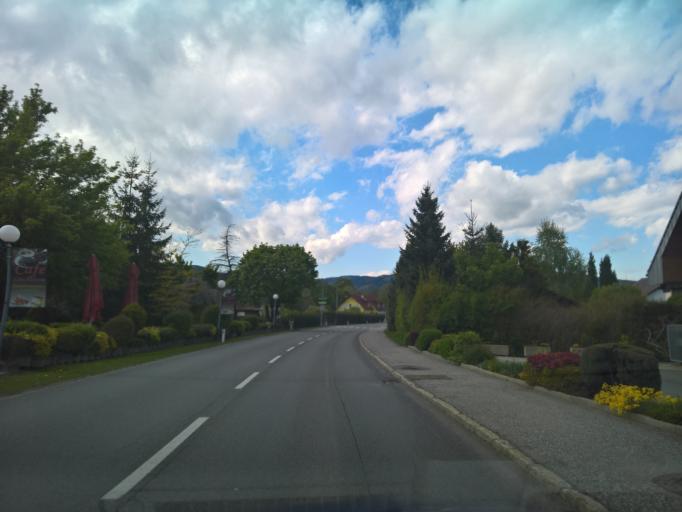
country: AT
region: Styria
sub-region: Politischer Bezirk Deutschlandsberg
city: Schwanberg
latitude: 46.7574
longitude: 15.2067
